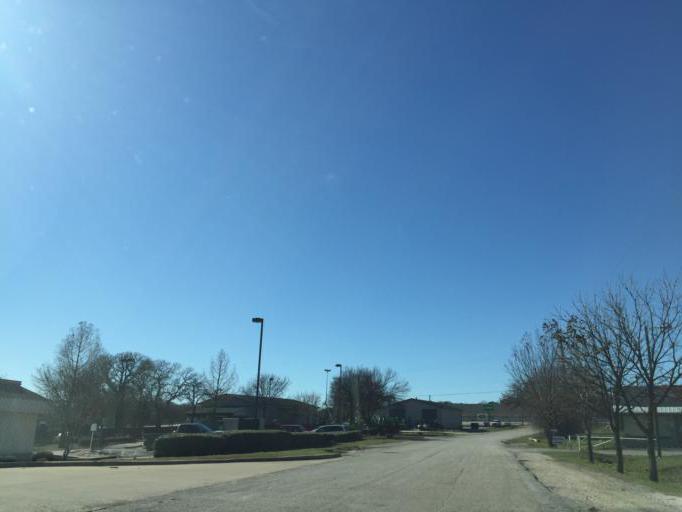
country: US
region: Texas
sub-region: Parker County
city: Weatherford
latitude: 32.7376
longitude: -97.7645
